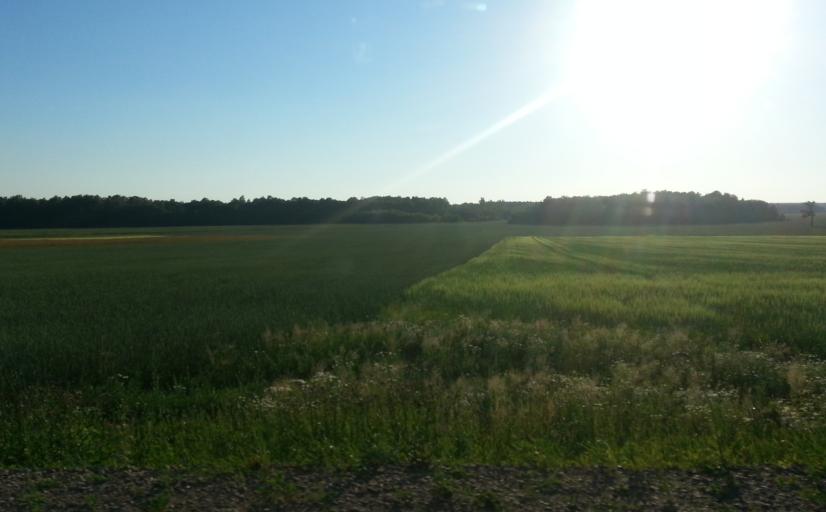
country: LT
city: Ramygala
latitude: 55.6050
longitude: 24.3478
